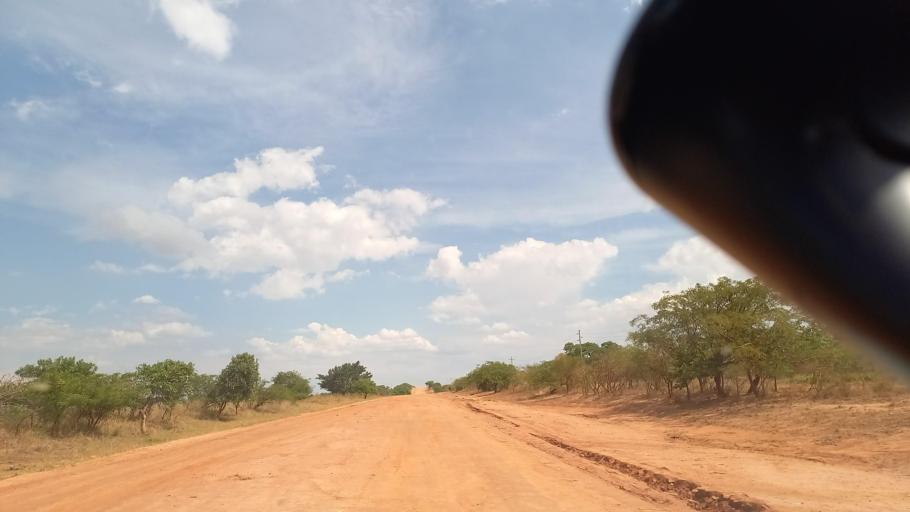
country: ZM
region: Lusaka
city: Kafue
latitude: -16.1246
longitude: 28.0430
